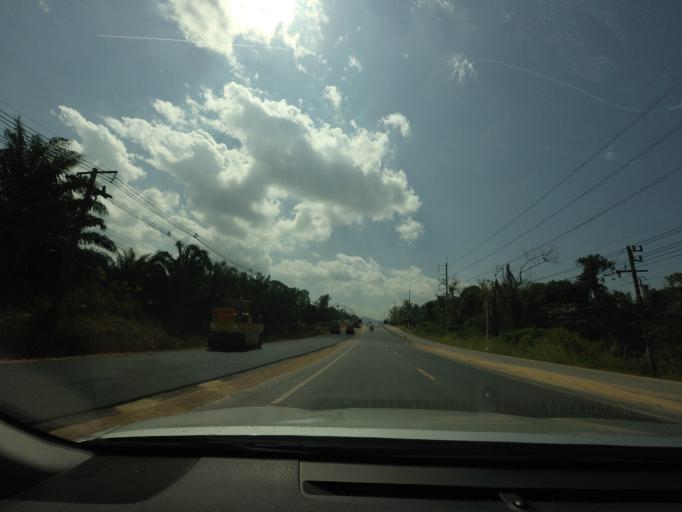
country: TH
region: Phangnga
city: Ban Khao Lak
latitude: 8.7183
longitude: 98.2569
